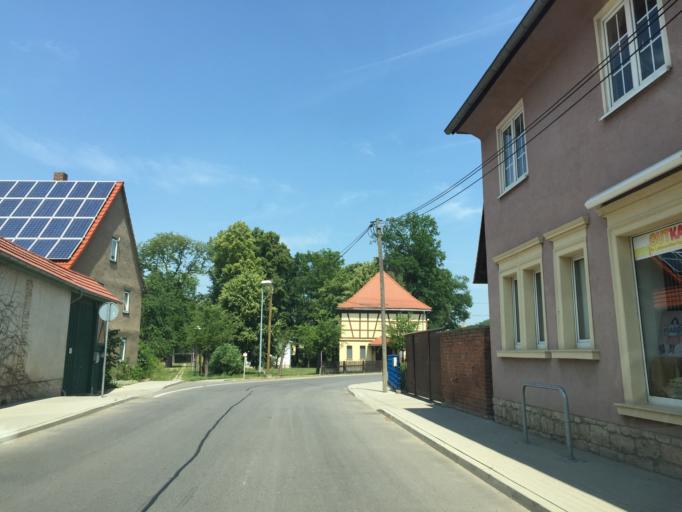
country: DE
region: Thuringia
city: Barchfeld
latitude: 50.8028
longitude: 11.1678
